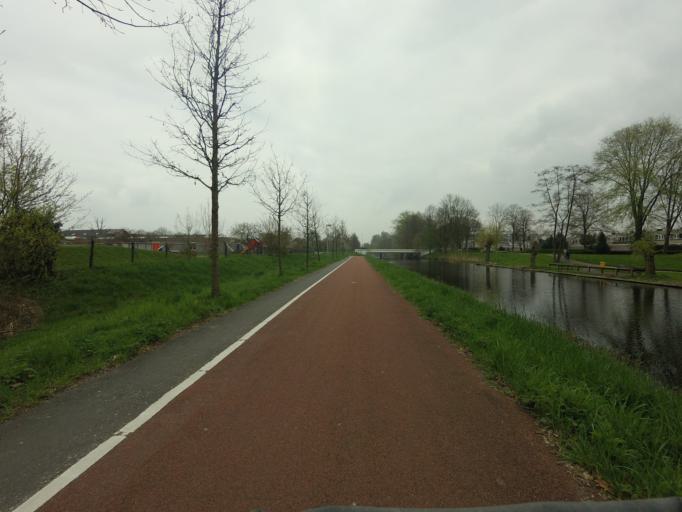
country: NL
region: Utrecht
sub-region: Gemeente Utrecht
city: Utrecht
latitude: 52.1202
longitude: 5.0922
